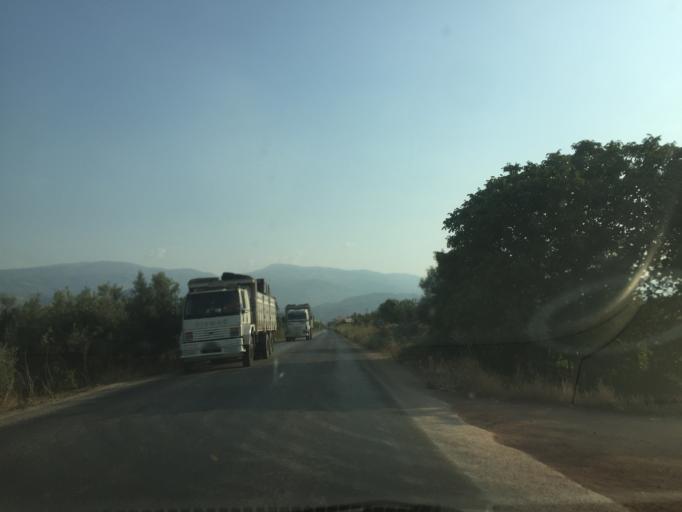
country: TR
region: Manisa
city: Salihli
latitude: 38.5017
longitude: 28.1856
